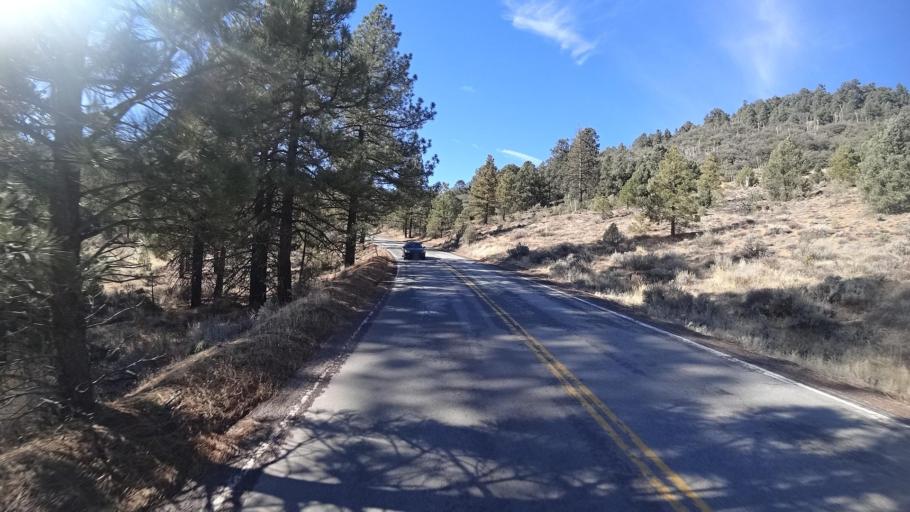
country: US
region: California
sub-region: Kern County
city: Pine Mountain Club
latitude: 34.8448
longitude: -119.0769
